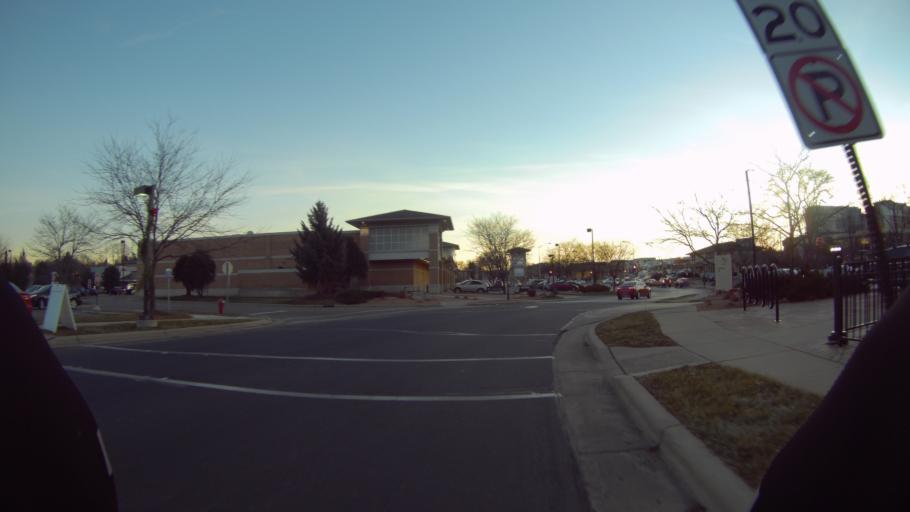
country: US
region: Wisconsin
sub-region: Dane County
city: Shorewood Hills
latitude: 43.0764
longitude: -89.4509
